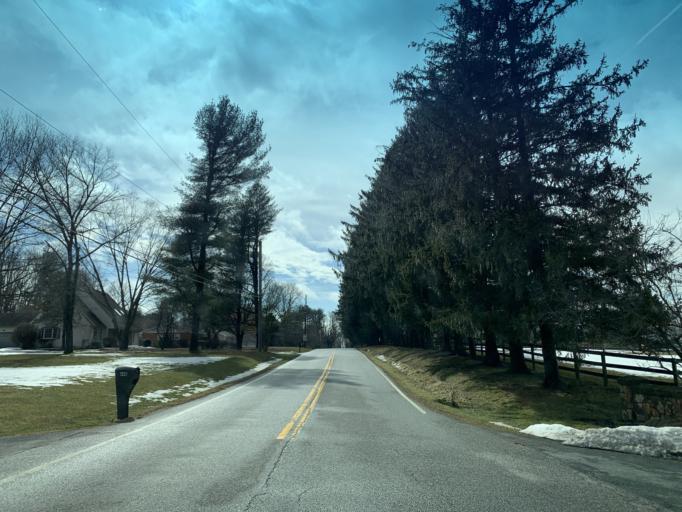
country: US
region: Delaware
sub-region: New Castle County
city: Newark
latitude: 39.7173
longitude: -75.7982
